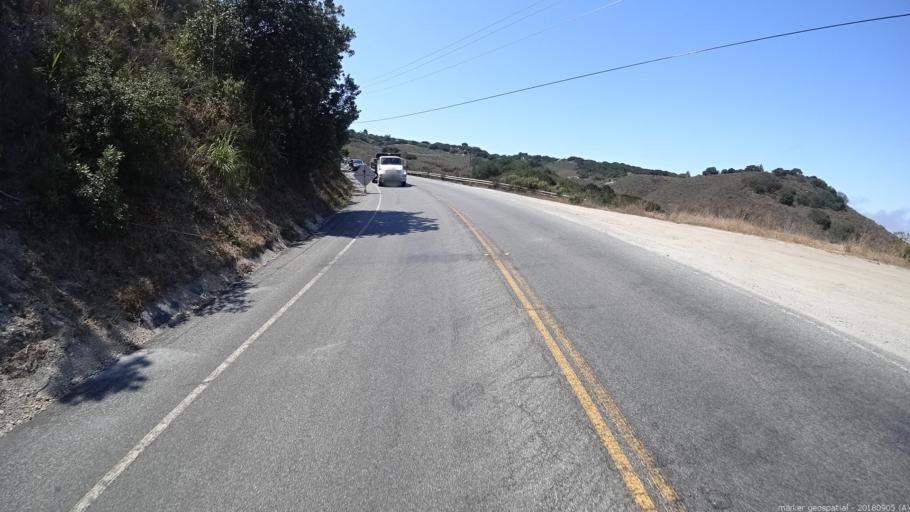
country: US
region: California
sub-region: Monterey County
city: Carmel Valley Village
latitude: 36.5562
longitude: -121.7539
